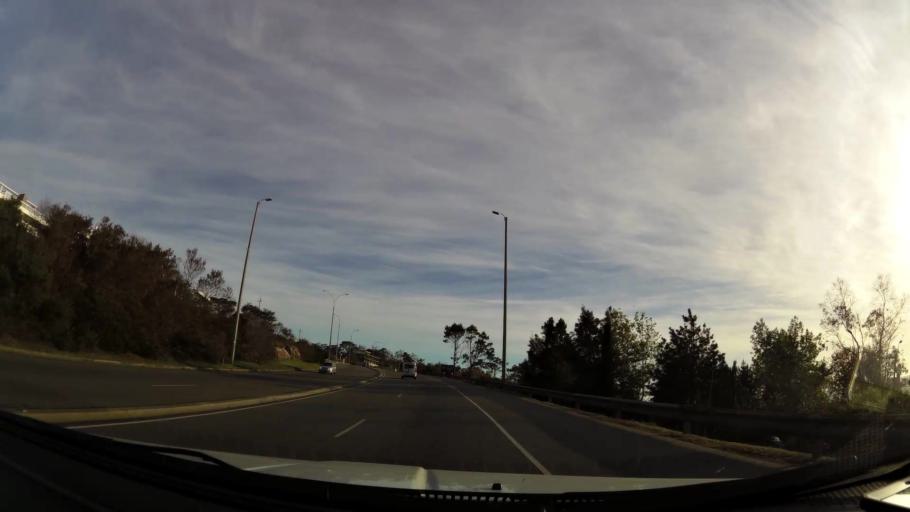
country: UY
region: Maldonado
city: Maldonado
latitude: -34.8906
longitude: -55.0384
